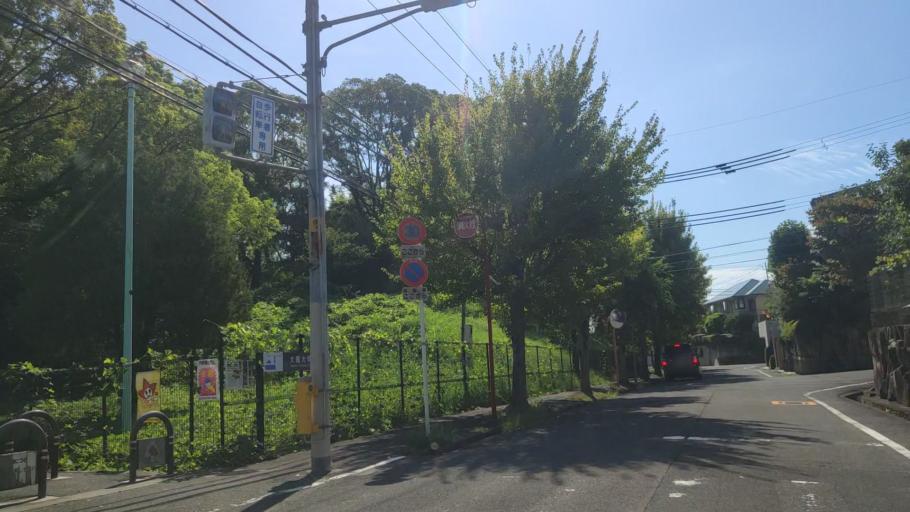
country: JP
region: Osaka
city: Mino
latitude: 34.8227
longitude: 135.5160
